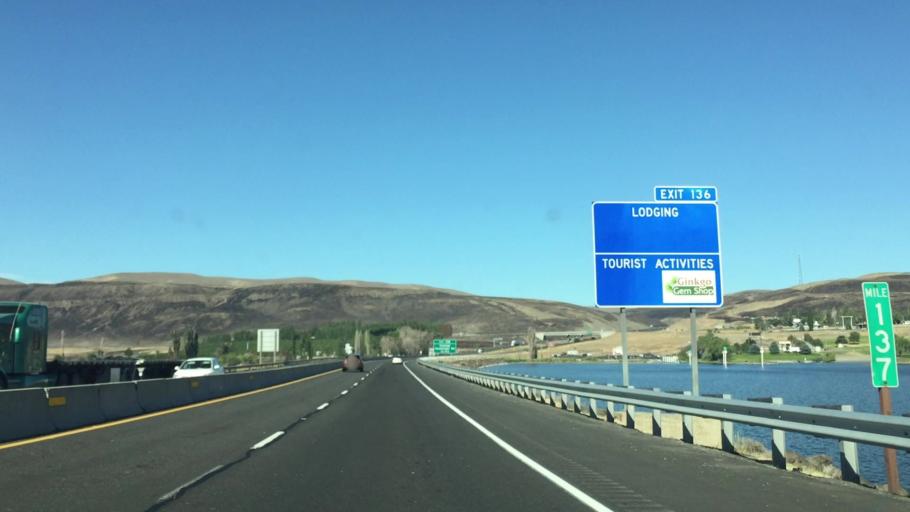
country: US
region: Washington
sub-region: Grant County
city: Mattawa
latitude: 46.9415
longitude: -119.9767
